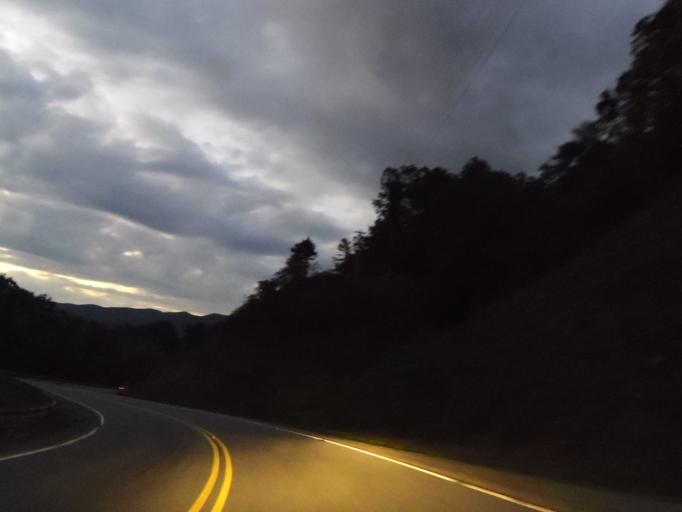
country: US
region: North Carolina
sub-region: Madison County
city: Marshall
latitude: 35.9082
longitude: -82.7503
